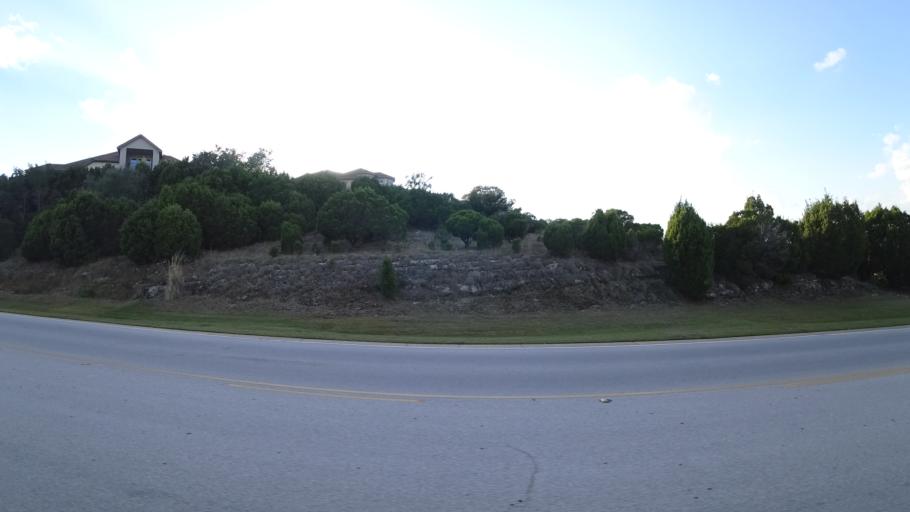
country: US
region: Texas
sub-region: Travis County
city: Barton Creek
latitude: 30.2924
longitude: -97.8623
